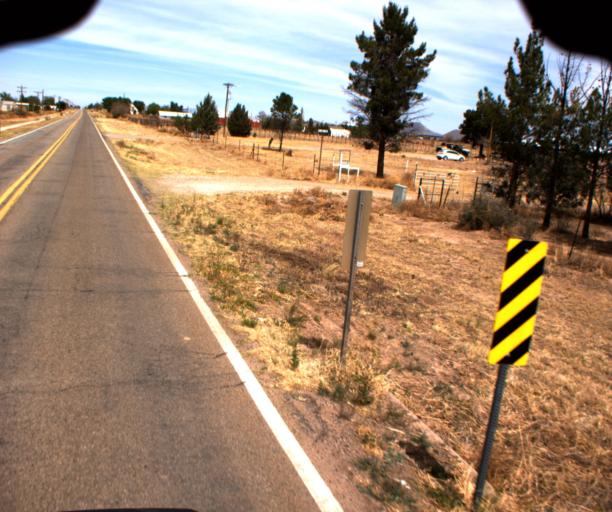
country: US
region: Arizona
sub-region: Cochise County
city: Bisbee
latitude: 31.6902
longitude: -109.6873
